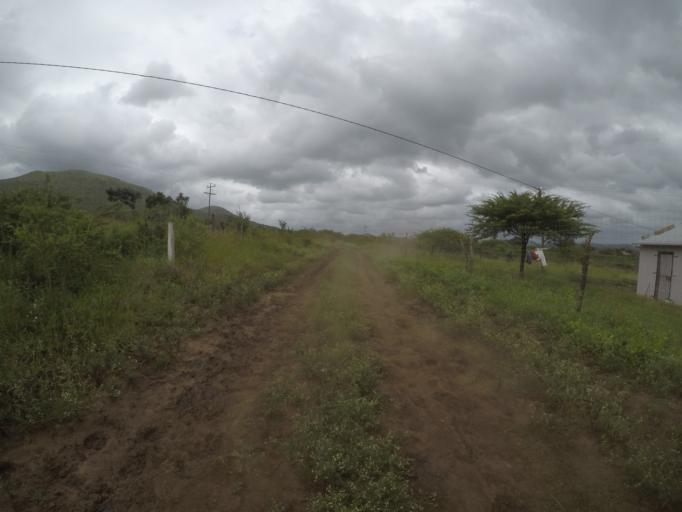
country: ZA
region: KwaZulu-Natal
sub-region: uThungulu District Municipality
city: Empangeni
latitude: -28.5614
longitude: 31.8782
